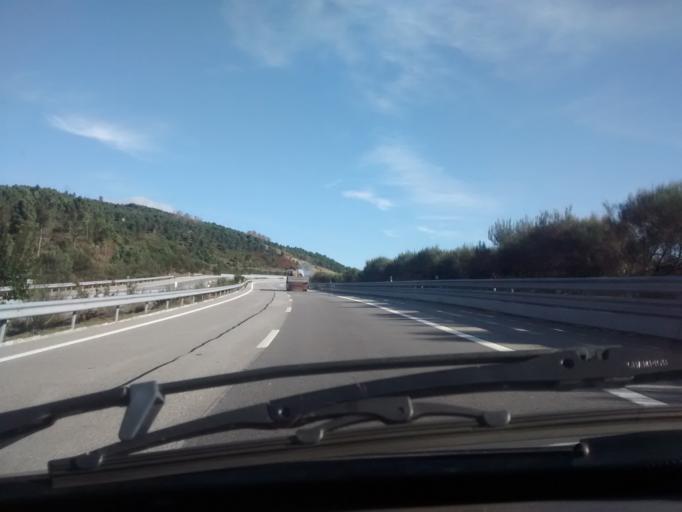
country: PT
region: Vila Real
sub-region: Ribeira de Pena
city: Ribeira de Pena
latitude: 41.4941
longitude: -7.8230
